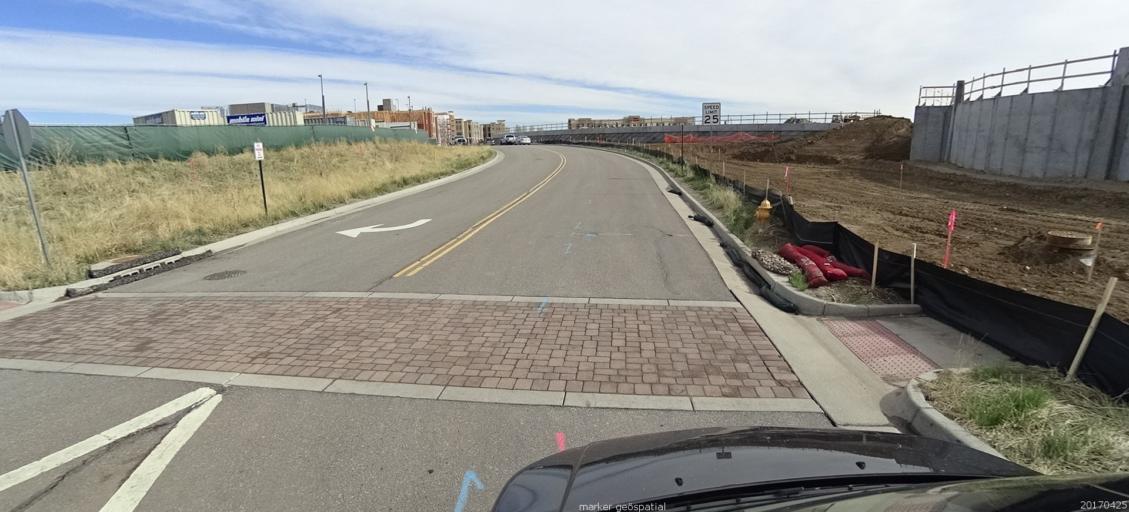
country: US
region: Colorado
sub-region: Douglas County
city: Meridian
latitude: 39.5321
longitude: -104.8712
